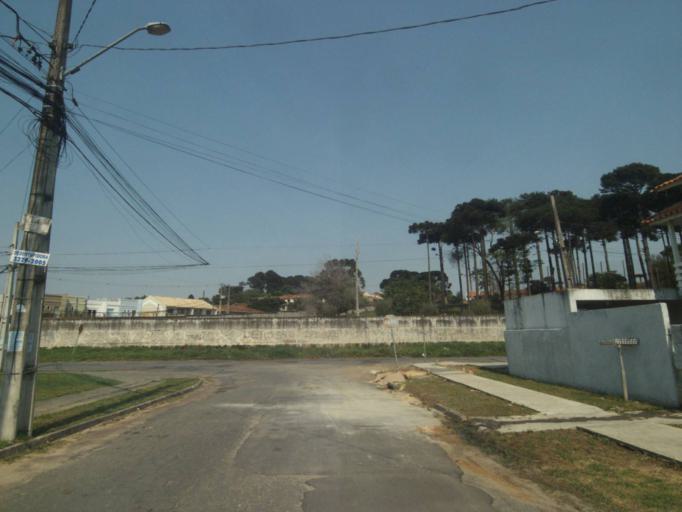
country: BR
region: Parana
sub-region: Sao Jose Dos Pinhais
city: Sao Jose dos Pinhais
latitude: -25.5193
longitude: -49.2498
